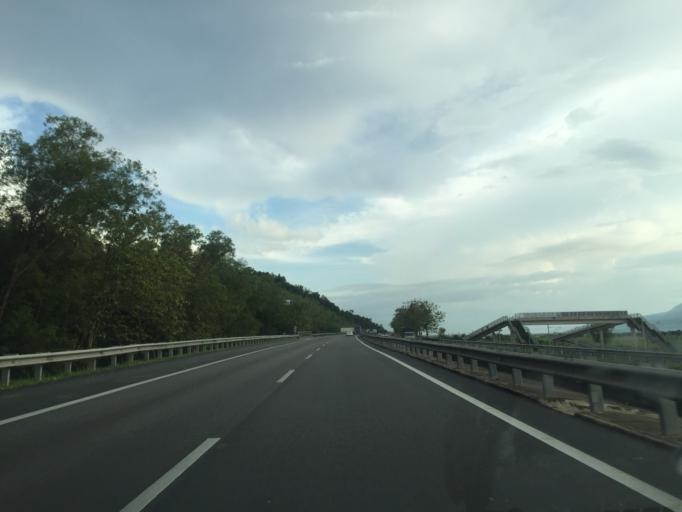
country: MY
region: Kedah
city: Gurun
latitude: 5.9440
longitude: 100.4572
